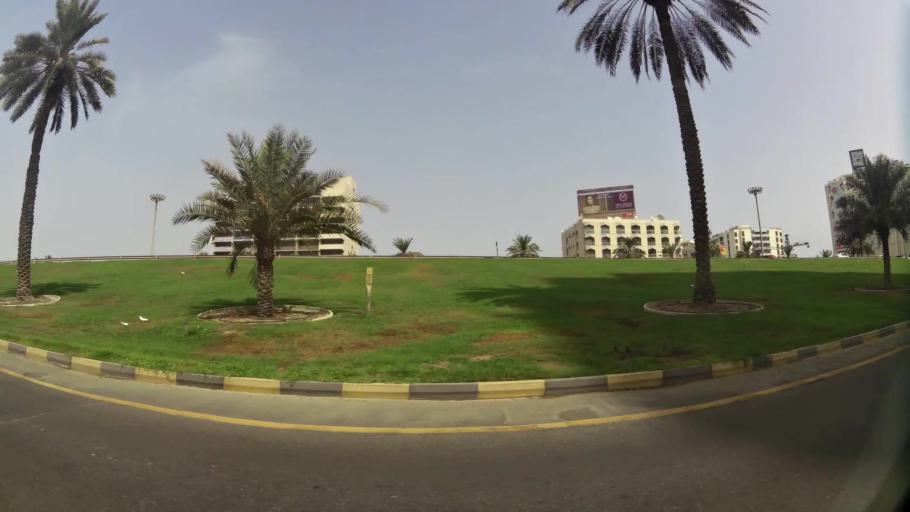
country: AE
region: Ash Shariqah
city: Sharjah
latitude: 25.3518
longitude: 55.3849
